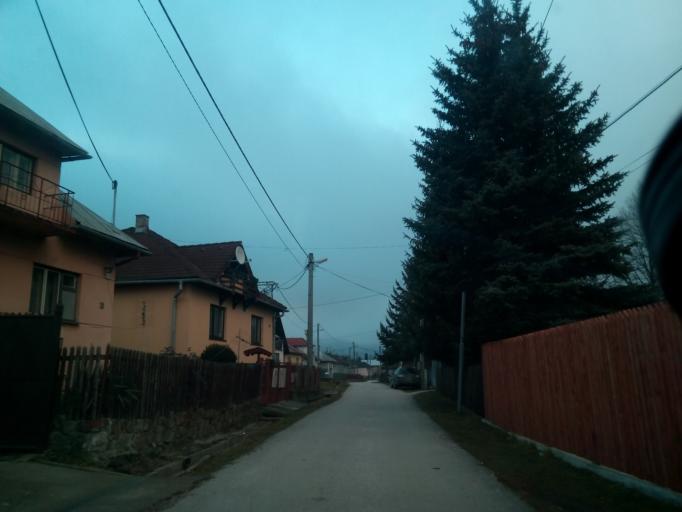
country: SK
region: Kosicky
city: Krompachy
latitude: 48.9273
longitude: 20.9208
